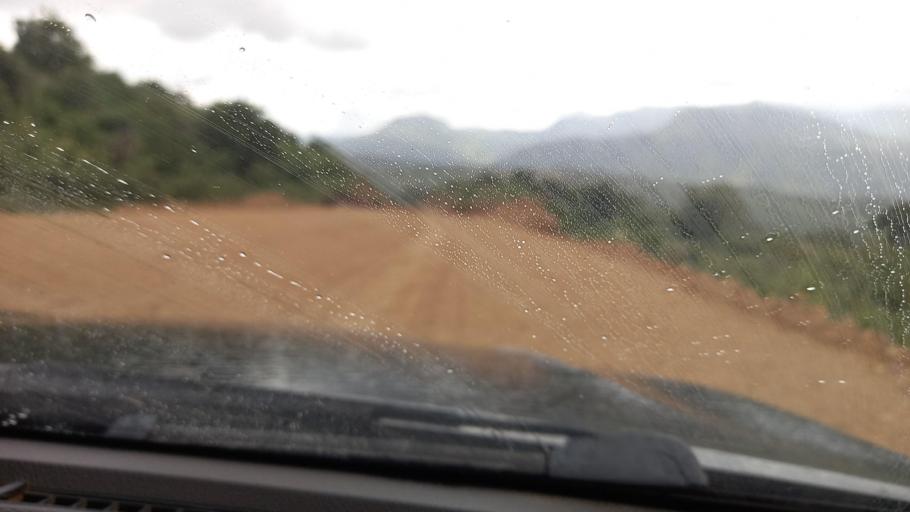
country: ET
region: Southern Nations, Nationalities, and People's Region
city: Mizan Teferi
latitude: 6.1742
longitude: 35.7098
